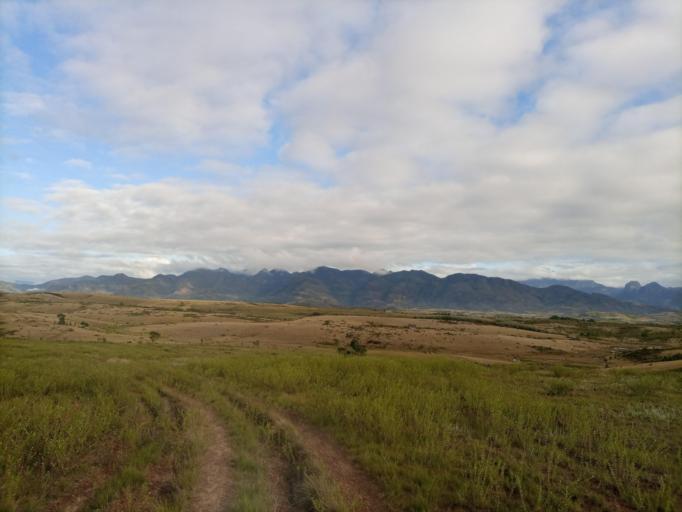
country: MG
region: Anosy
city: Fort Dauphin
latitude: -24.3086
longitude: 47.2476
